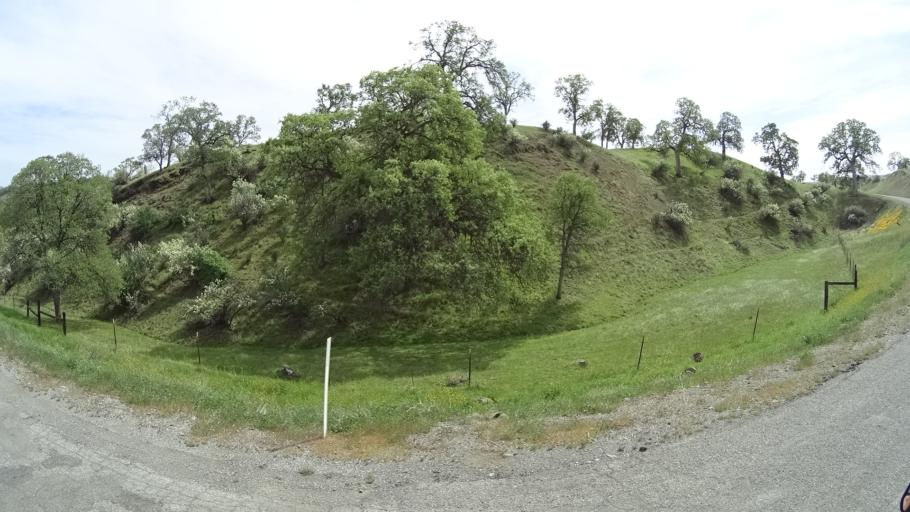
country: US
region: California
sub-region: Glenn County
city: Willows
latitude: 39.6126
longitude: -122.5799
